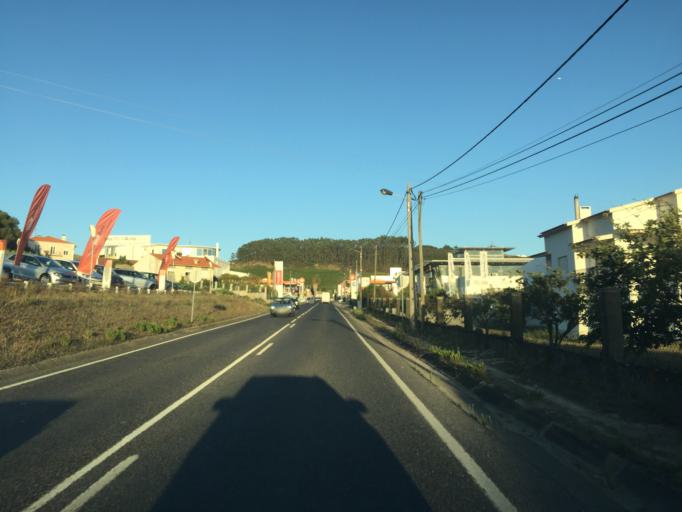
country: PT
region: Lisbon
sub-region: Torres Vedras
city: Torres Vedras
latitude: 39.0710
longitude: -9.2467
